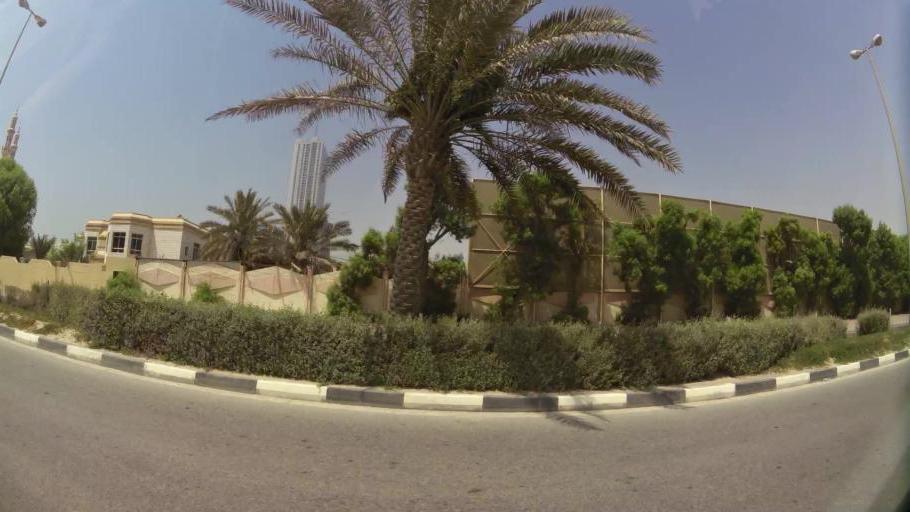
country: AE
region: Ajman
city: Ajman
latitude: 25.3989
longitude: 55.4278
